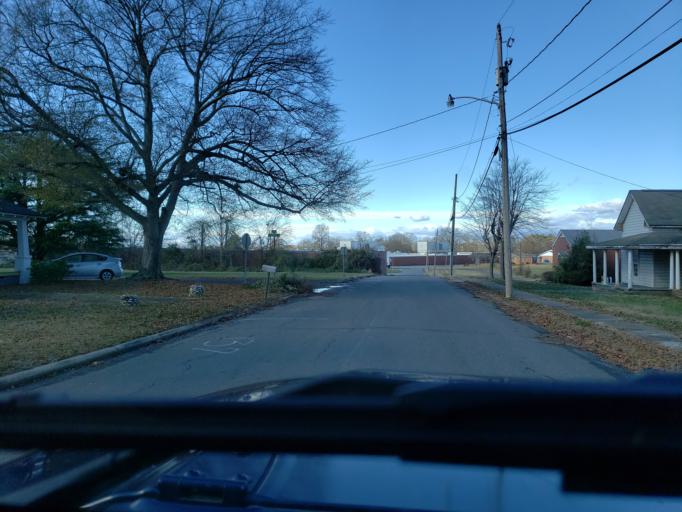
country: US
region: North Carolina
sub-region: Cleveland County
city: White Plains
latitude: 35.1706
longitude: -81.4500
